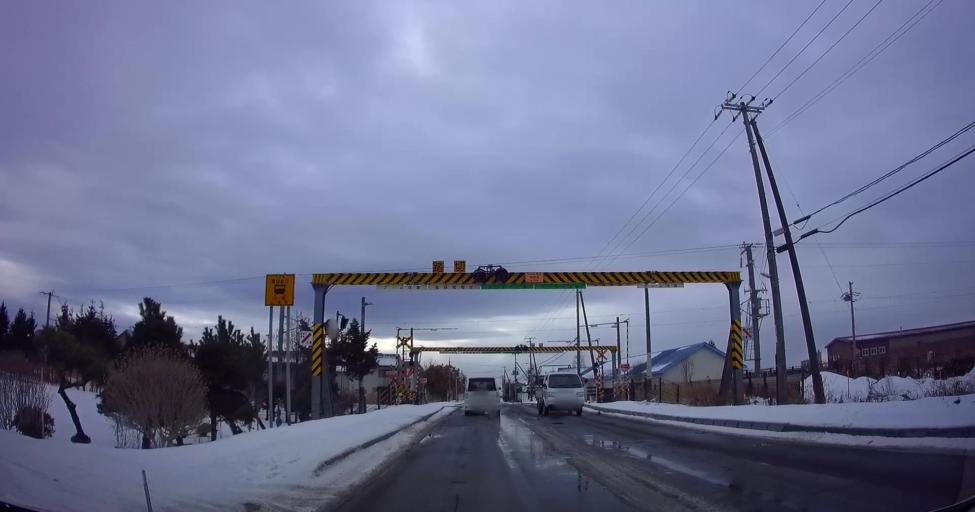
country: JP
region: Hokkaido
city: Kamiiso
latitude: 41.8258
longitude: 140.6856
